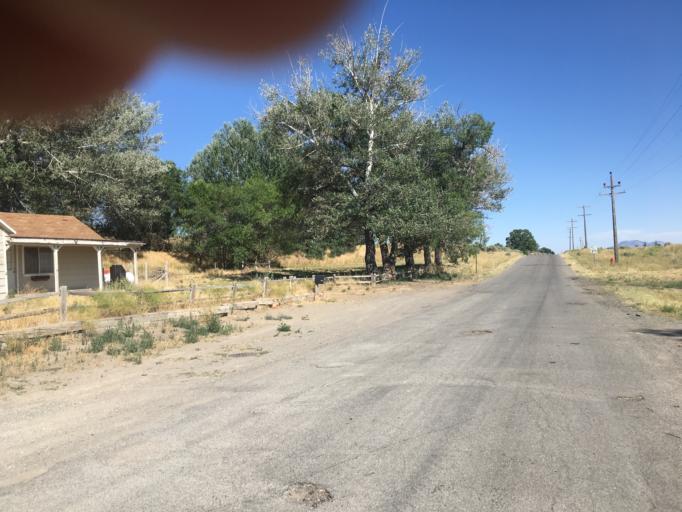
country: US
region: Idaho
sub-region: Butte County
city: Arco
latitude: 43.6327
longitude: -113.2937
